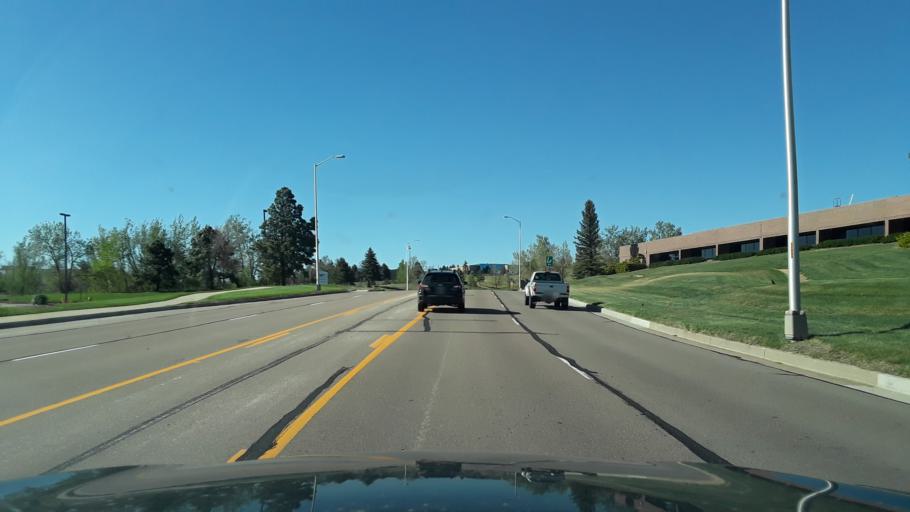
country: US
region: Colorado
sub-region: El Paso County
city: Air Force Academy
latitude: 38.9536
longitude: -104.7920
